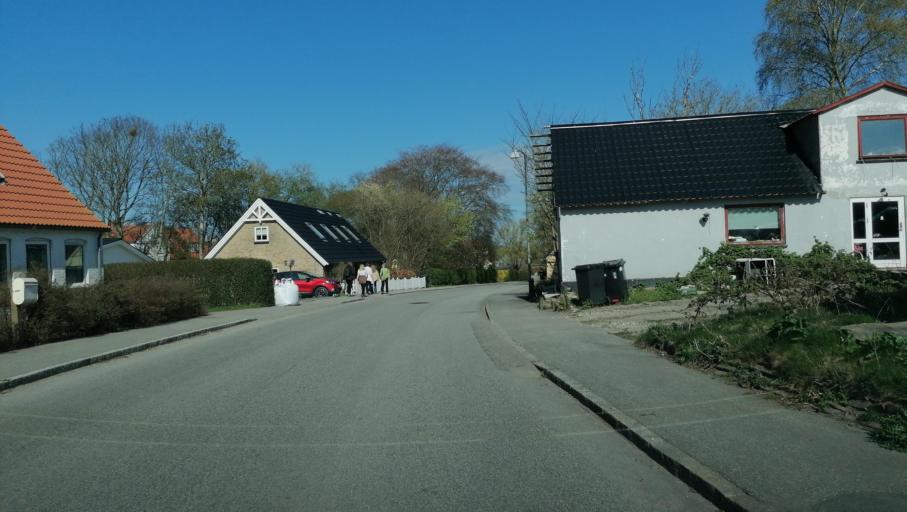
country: DK
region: Zealand
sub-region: Holbaek Kommune
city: Jyderup
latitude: 55.7205
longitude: 11.3843
